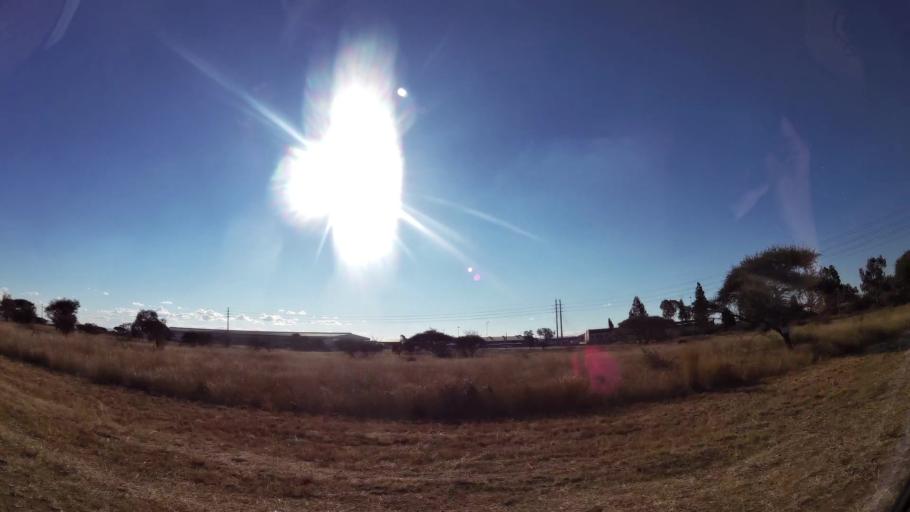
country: ZA
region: Limpopo
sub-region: Capricorn District Municipality
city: Polokwane
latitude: -23.8714
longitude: 29.4838
